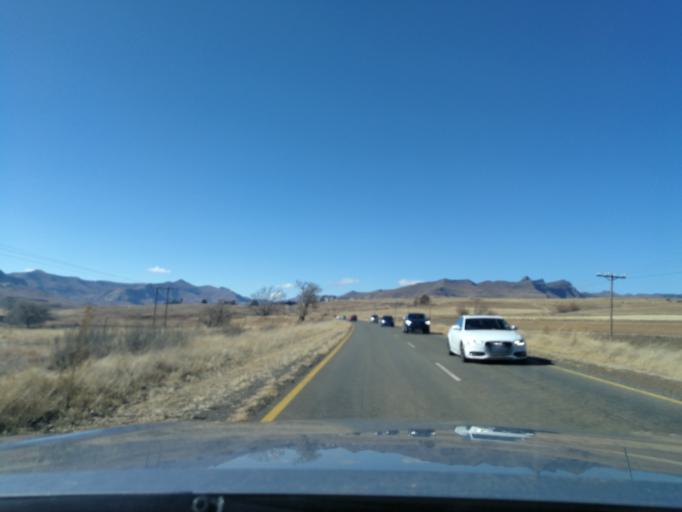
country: ZA
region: Orange Free State
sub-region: Thabo Mofutsanyana District Municipality
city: Phuthaditjhaba
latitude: -28.5268
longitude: 28.4857
